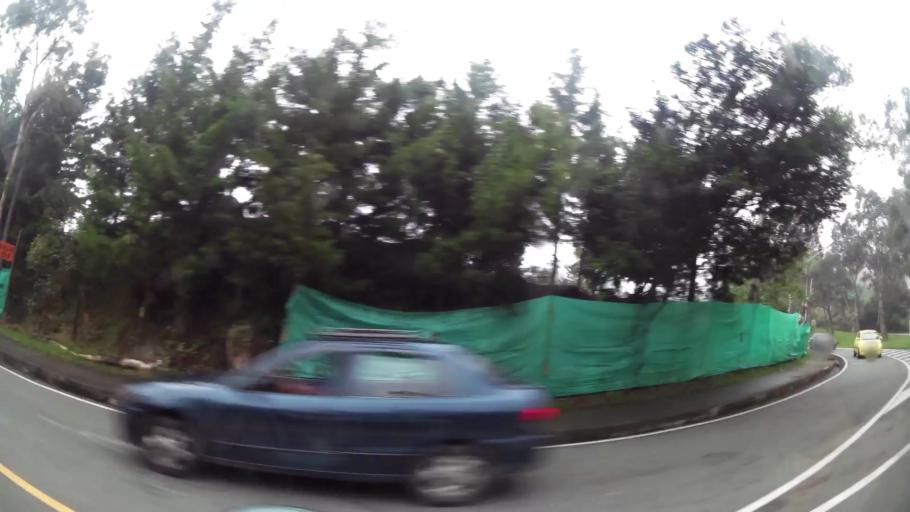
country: CO
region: Antioquia
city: Envigado
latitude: 6.1833
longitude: -75.5465
